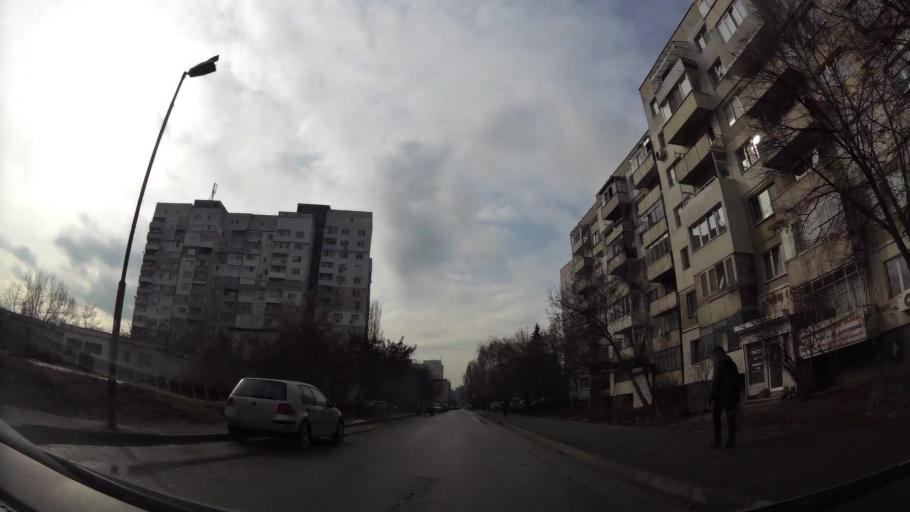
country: BG
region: Sofia-Capital
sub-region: Stolichna Obshtina
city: Sofia
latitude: 42.7156
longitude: 23.2751
